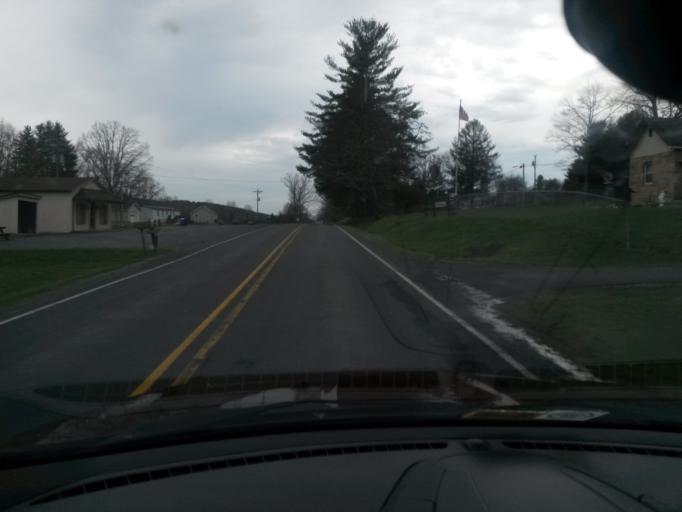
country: US
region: Virginia
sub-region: Bath County
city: Warm Springs
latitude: 38.0956
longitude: -79.7787
